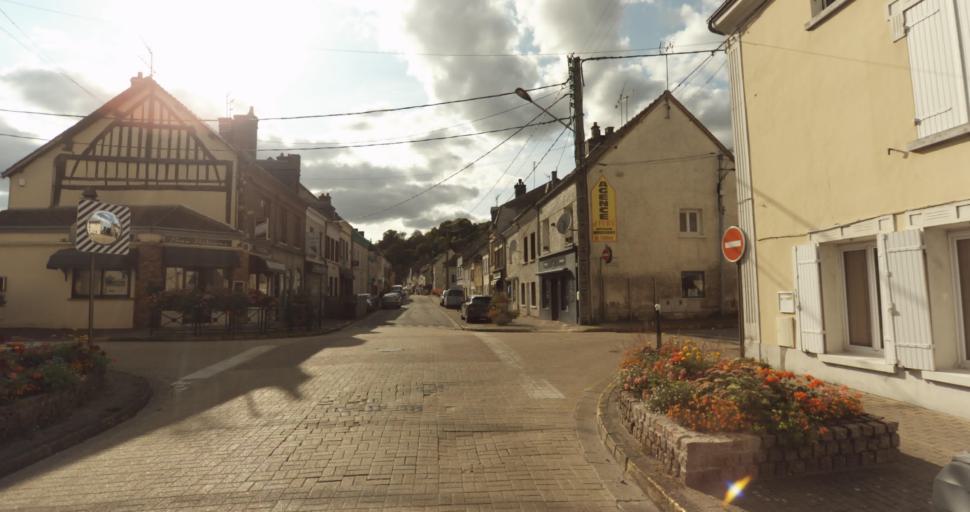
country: FR
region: Haute-Normandie
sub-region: Departement de l'Eure
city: Ivry-la-Bataille
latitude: 48.8831
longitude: 1.4622
